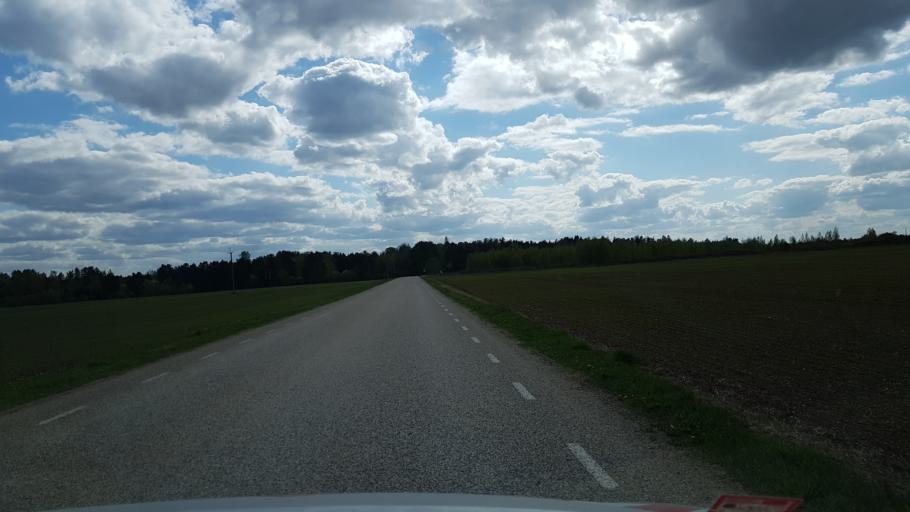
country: EE
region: Tartu
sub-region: Tartu linn
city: Tartu
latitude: 58.3496
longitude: 26.8485
